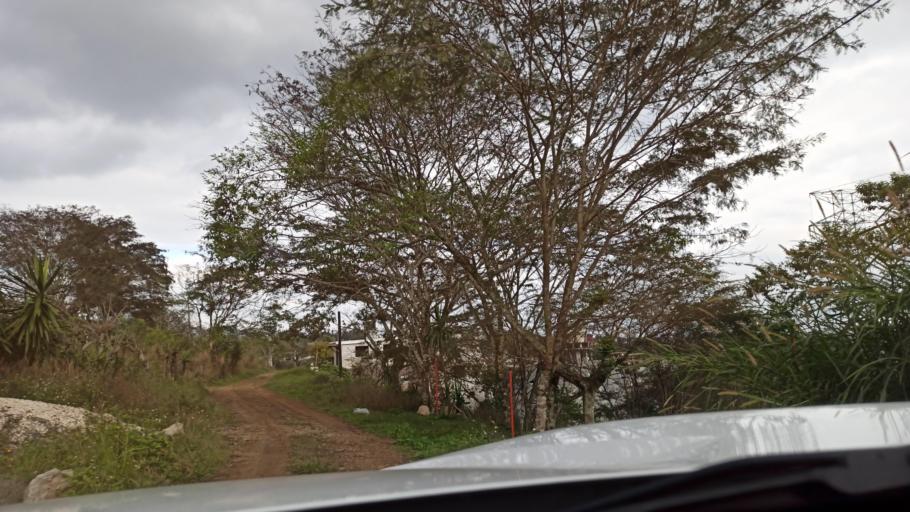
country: MX
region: Veracruz
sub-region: Fortin
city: Fortin de las Flores
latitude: 18.9153
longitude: -97.0023
